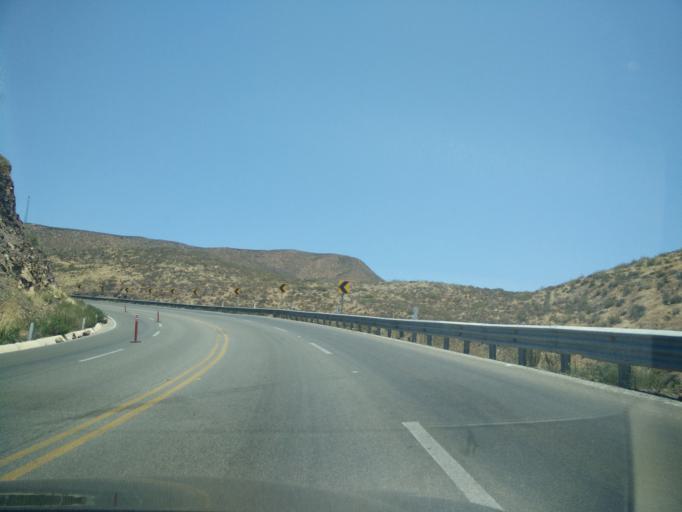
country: MX
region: Baja California
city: El Sauzal
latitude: 31.9293
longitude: -116.6679
